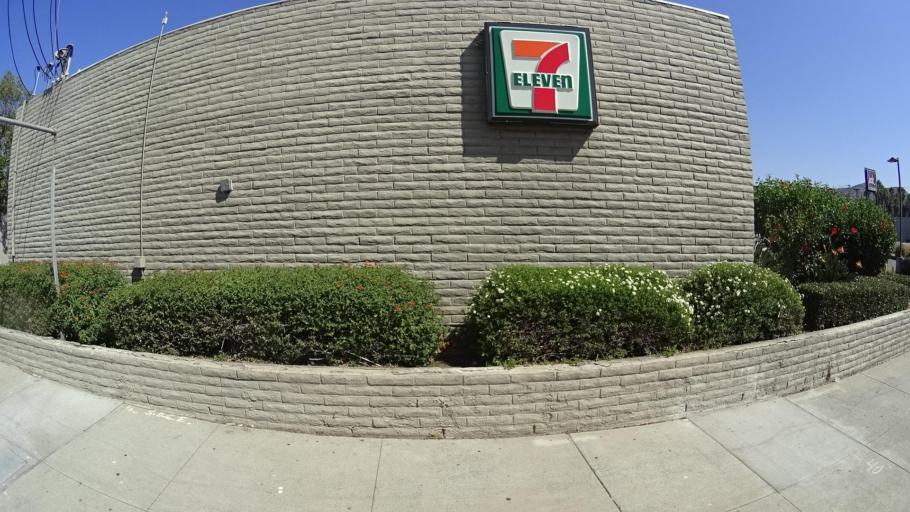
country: US
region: California
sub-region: San Diego County
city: Granite Hills
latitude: 32.8127
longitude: -116.9195
